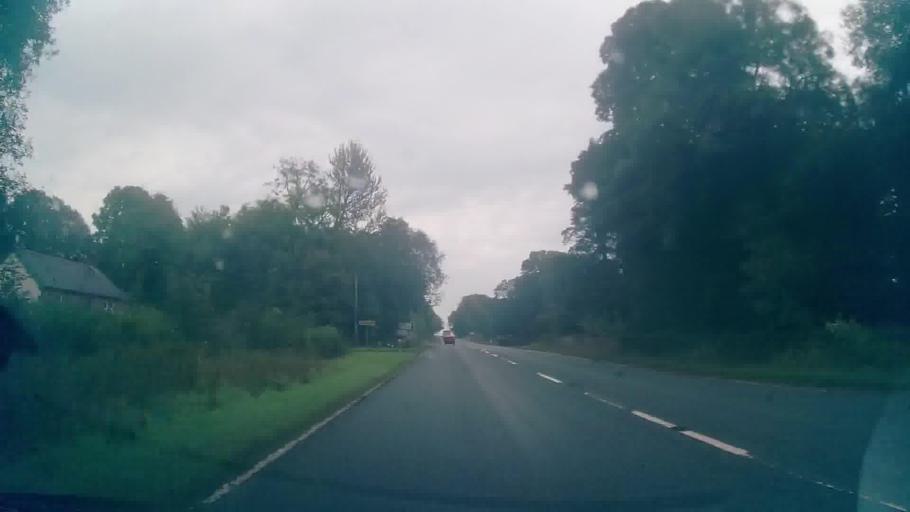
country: GB
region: Scotland
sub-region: Dumfries and Galloway
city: Annan
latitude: 55.0094
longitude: -3.3398
